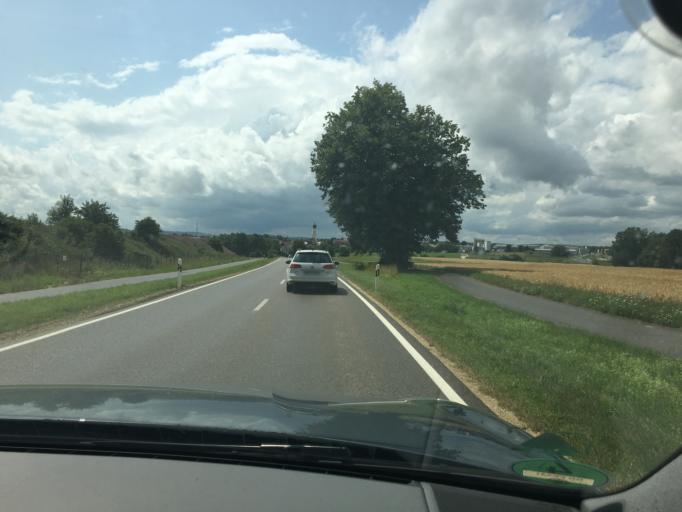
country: DE
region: Baden-Wuerttemberg
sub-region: Tuebingen Region
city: Merklingen
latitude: 48.5133
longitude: 9.7734
